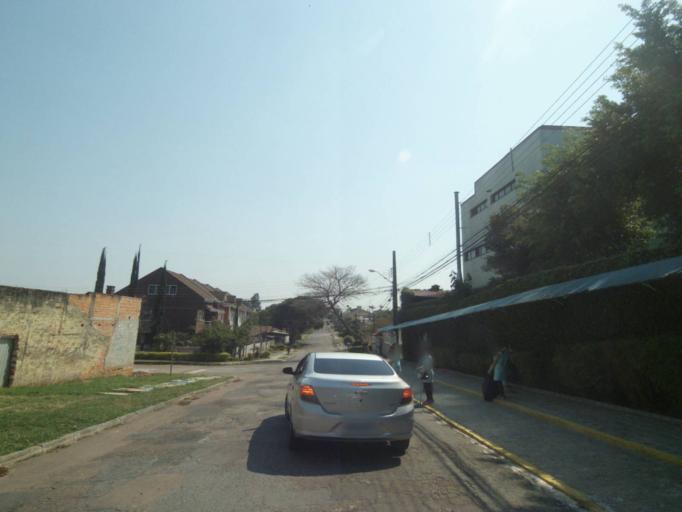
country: BR
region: Parana
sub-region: Sao Jose Dos Pinhais
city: Sao Jose dos Pinhais
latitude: -25.5064
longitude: -49.2747
